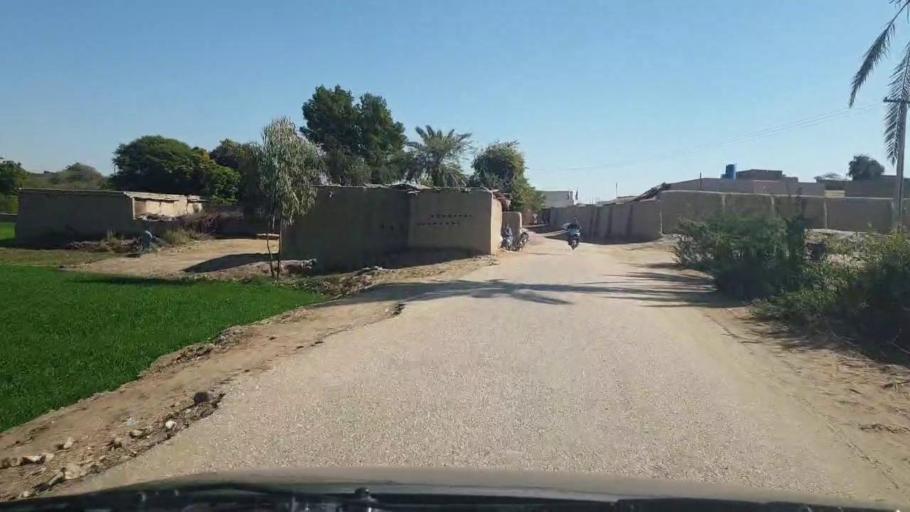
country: PK
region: Sindh
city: Bozdar
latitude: 27.0595
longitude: 68.6367
